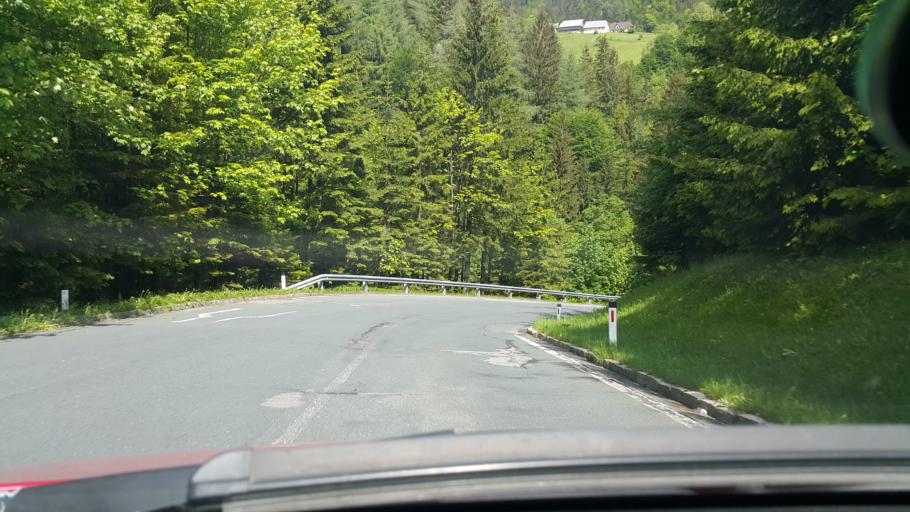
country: AT
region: Carinthia
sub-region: Politischer Bezirk Klagenfurt Land
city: Ferlach
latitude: 46.4523
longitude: 14.2560
